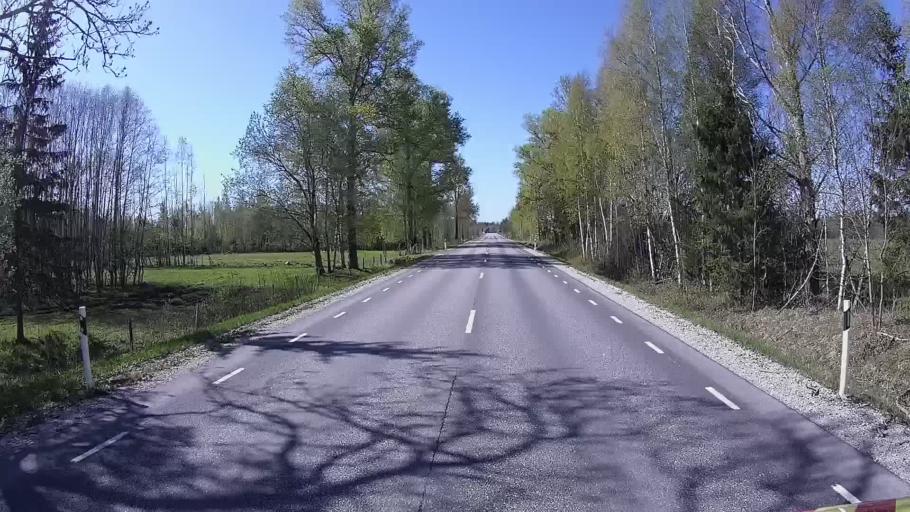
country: EE
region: Raplamaa
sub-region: Jaervakandi vald
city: Jarvakandi
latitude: 58.7406
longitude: 24.8080
